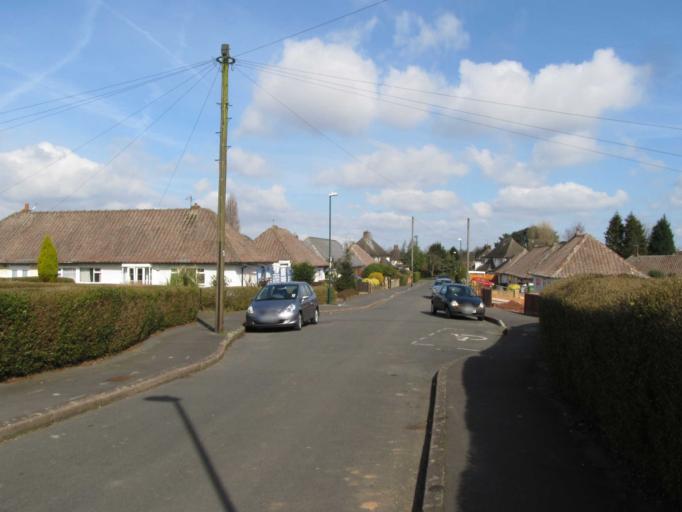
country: GB
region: England
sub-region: Nottingham
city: Nottingham
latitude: 52.9489
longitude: -1.1926
